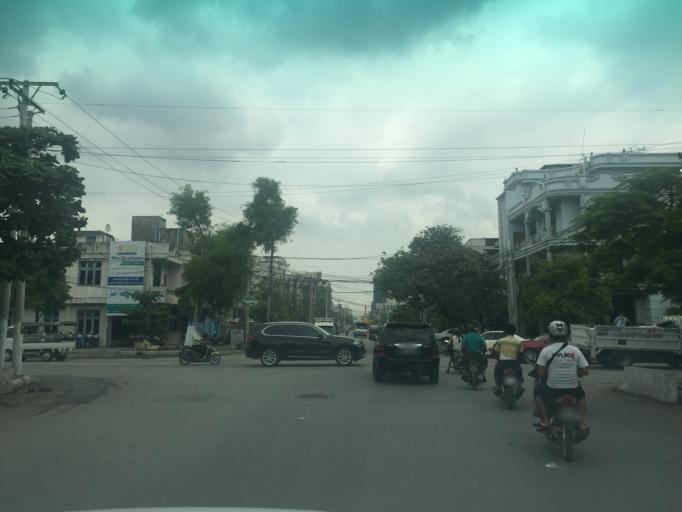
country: MM
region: Mandalay
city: Mandalay
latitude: 21.9644
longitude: 96.0817
